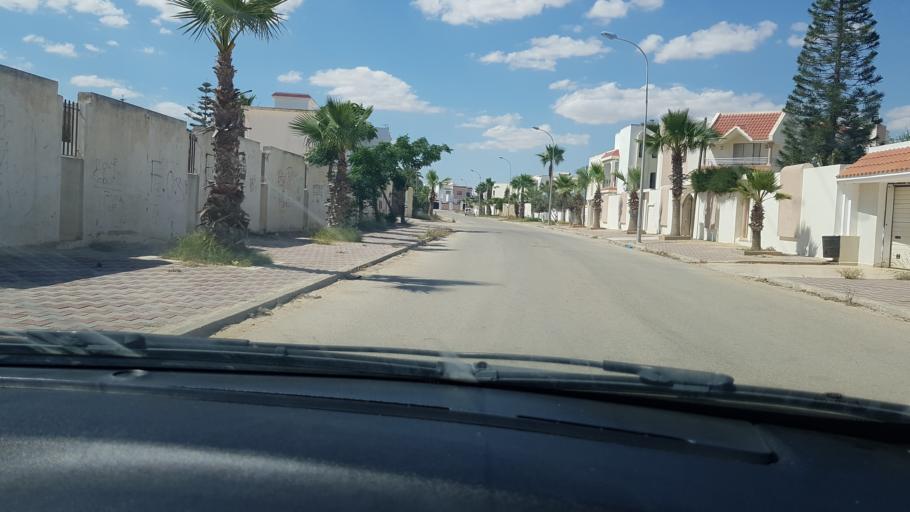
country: TN
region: Safaqis
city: Al Qarmadah
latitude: 34.8289
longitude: 10.7598
